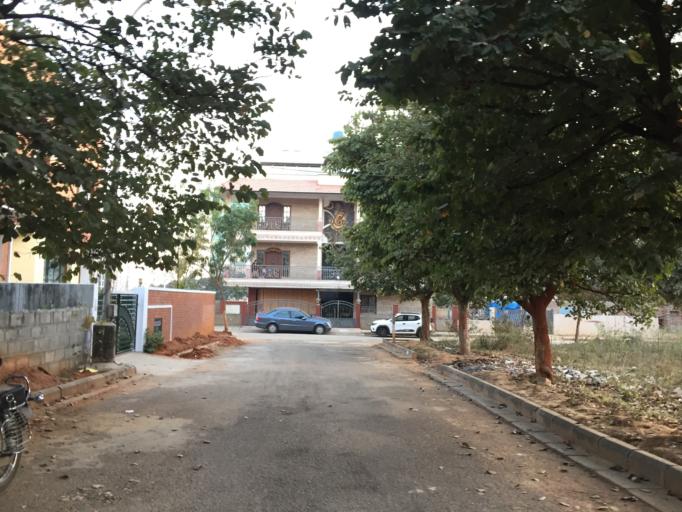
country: IN
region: Karnataka
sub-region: Bangalore Urban
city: Yelahanka
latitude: 13.0523
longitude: 77.6237
